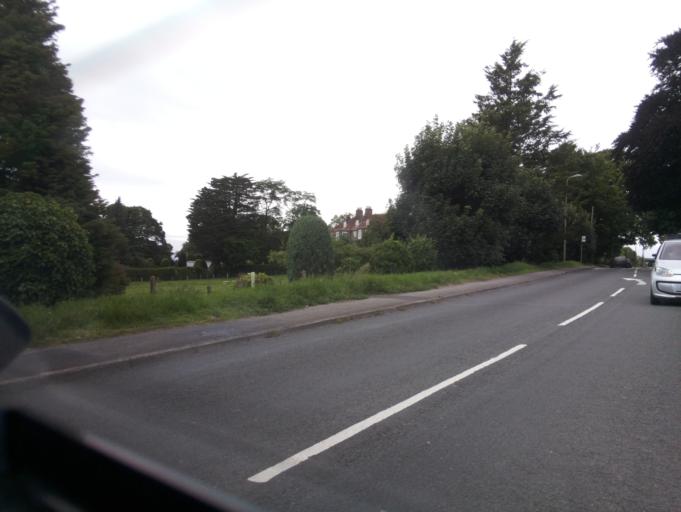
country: GB
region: England
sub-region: North Somerset
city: Congresbury
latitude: 51.3798
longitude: -2.8103
